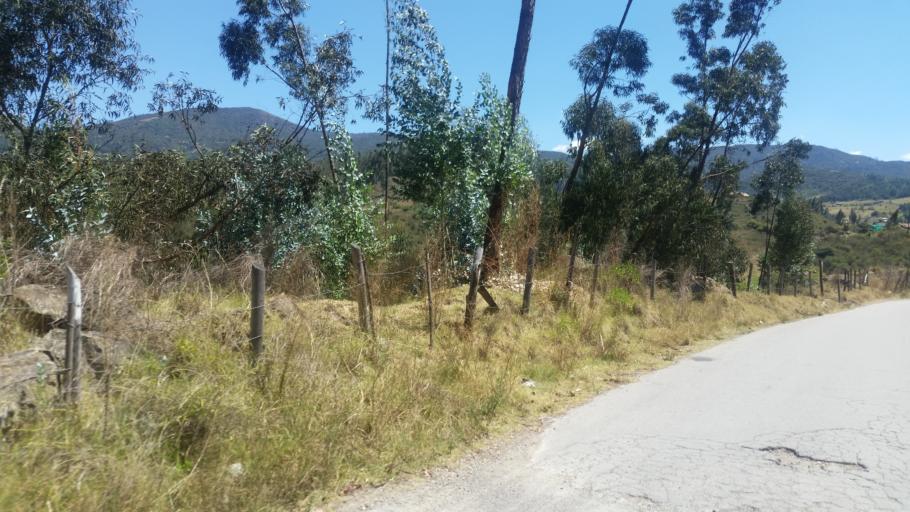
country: CO
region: Boyaca
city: Topaga
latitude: 5.7583
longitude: -72.8526
